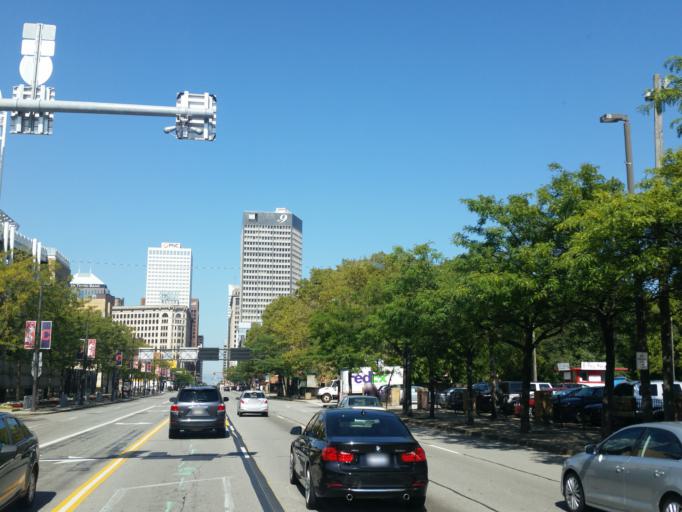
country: US
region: Ohio
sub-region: Cuyahoga County
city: Cleveland
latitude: 41.4960
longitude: -81.6829
